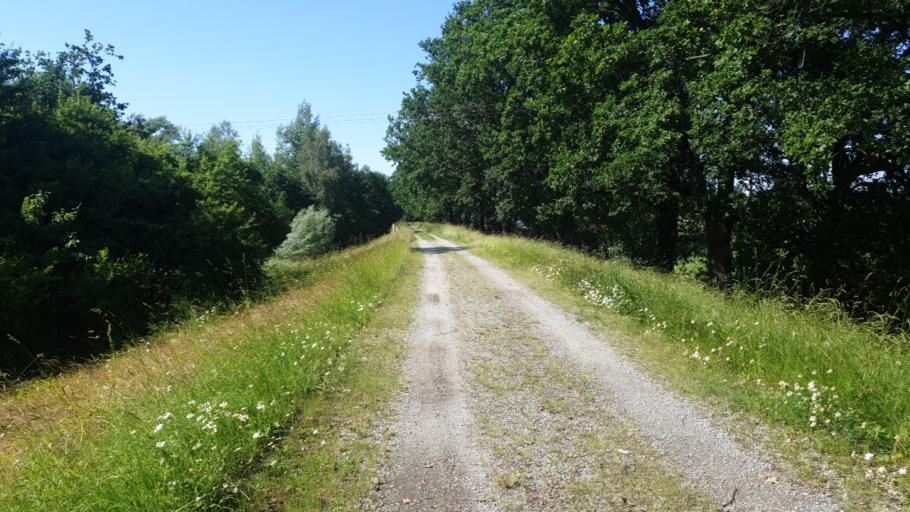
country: PL
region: Lower Silesian Voivodeship
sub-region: Powiat wroclawski
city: Radwanice
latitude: 51.0912
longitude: 17.1154
